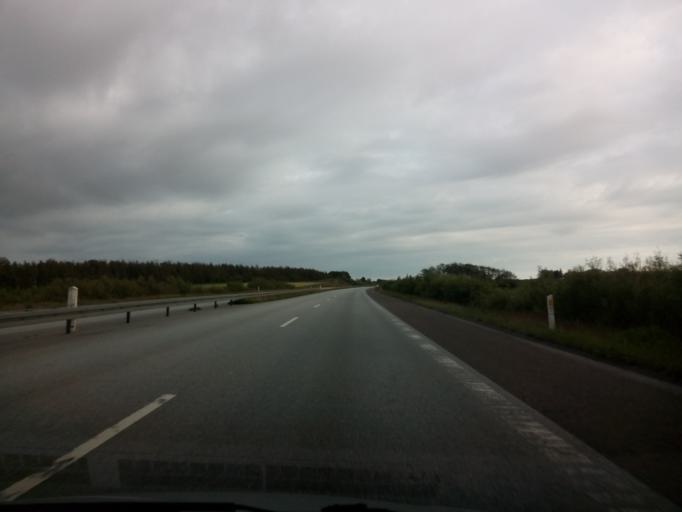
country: DK
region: North Denmark
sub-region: Hjorring Kommune
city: Hjorring
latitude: 57.4025
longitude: 10.0296
